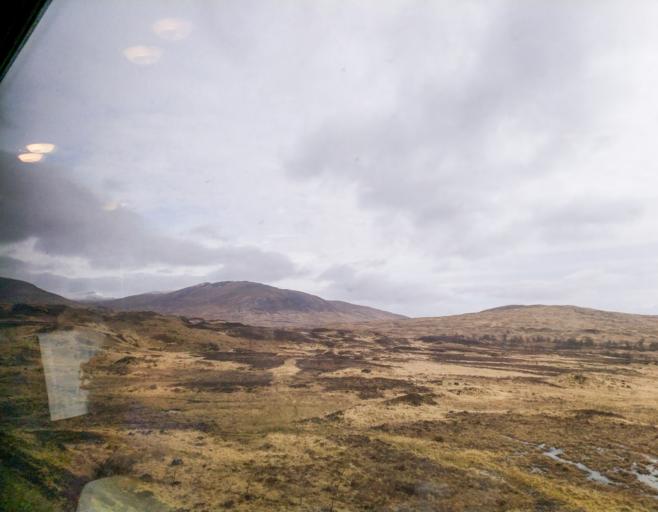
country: GB
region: Scotland
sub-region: Highland
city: Spean Bridge
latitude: 56.6886
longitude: -4.5765
